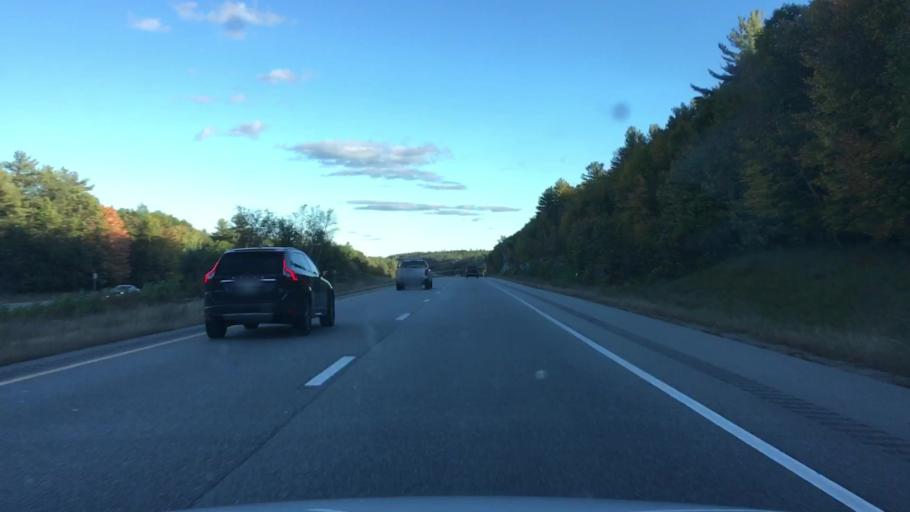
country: US
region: New Hampshire
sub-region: Rockingham County
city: Candia
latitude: 43.0403
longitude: -71.2646
